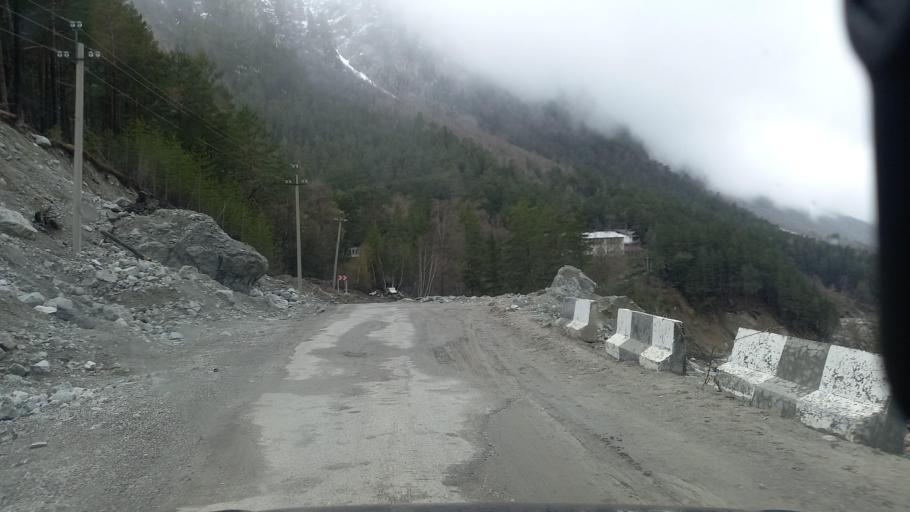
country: RU
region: Kabardino-Balkariya
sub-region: El'brusskiy Rayon
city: El'brus
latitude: 43.2288
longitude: 42.6570
